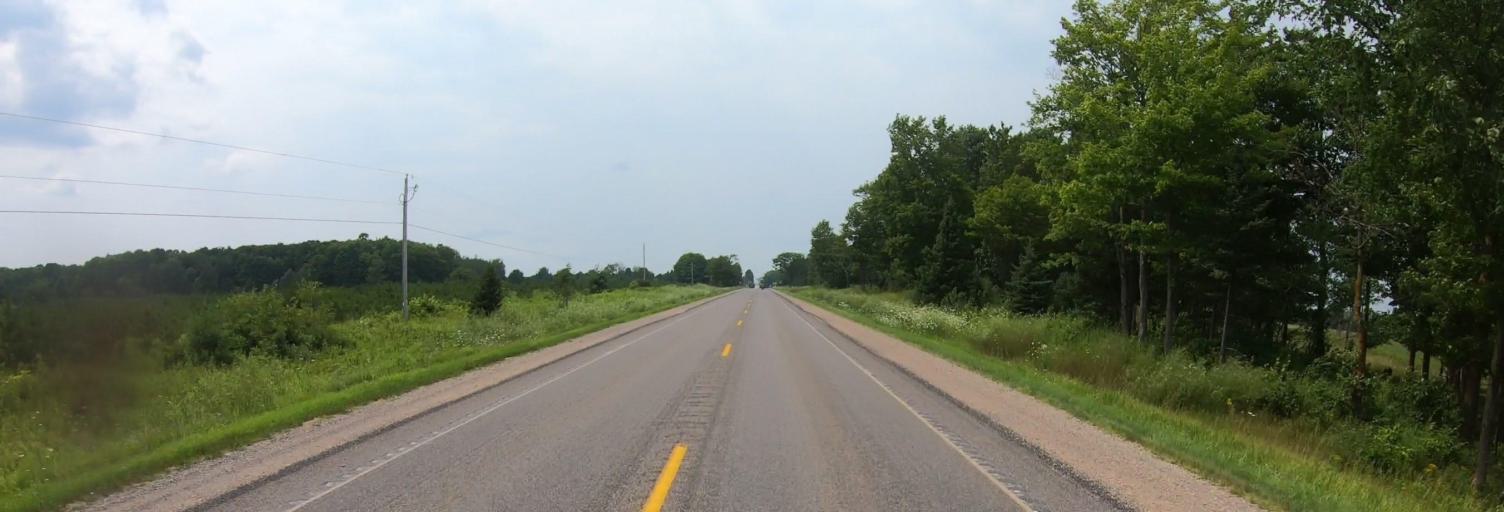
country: US
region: Michigan
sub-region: Alger County
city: Munising
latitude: 46.3331
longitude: -86.9190
